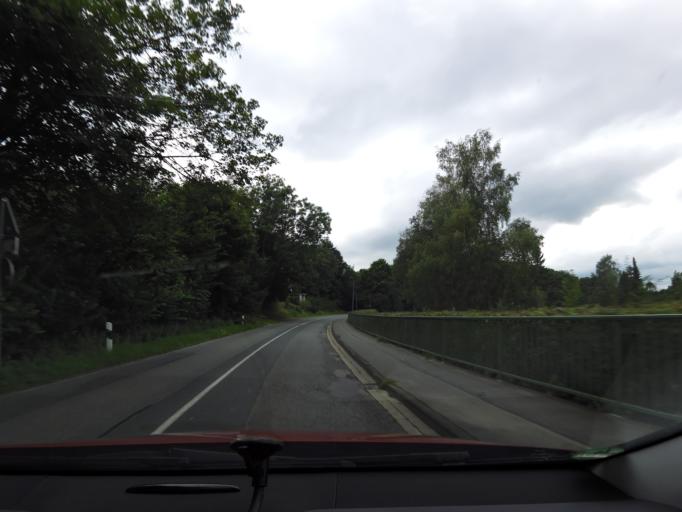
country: DE
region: Lower Saxony
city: Bad Harzburg
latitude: 51.8857
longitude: 10.5916
